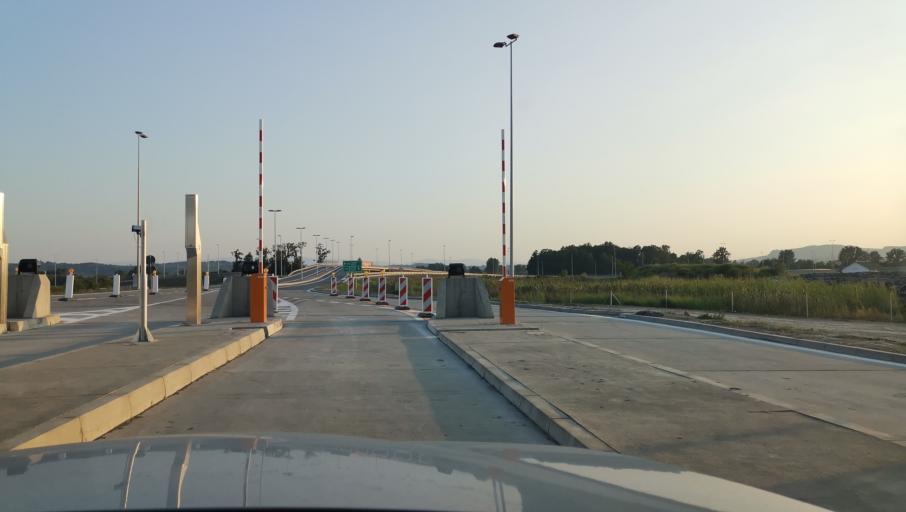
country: RS
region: Central Serbia
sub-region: Kolubarski Okrug
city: Lajkovac
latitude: 44.3598
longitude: 20.1308
